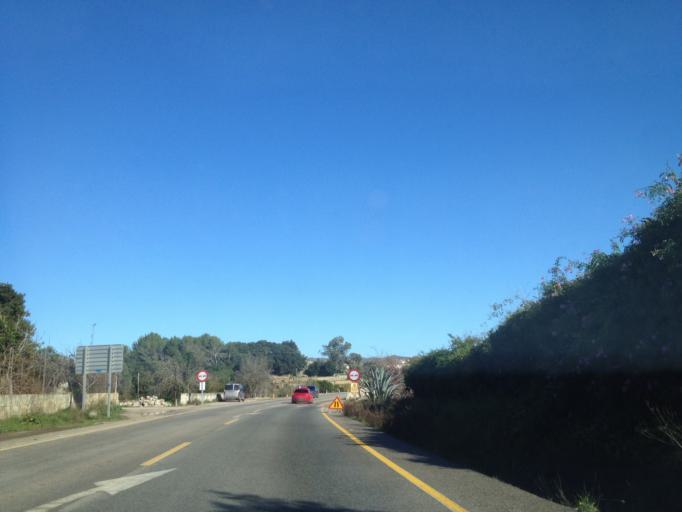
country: ES
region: Balearic Islands
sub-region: Illes Balears
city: Arta
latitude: 39.6865
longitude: 3.3439
